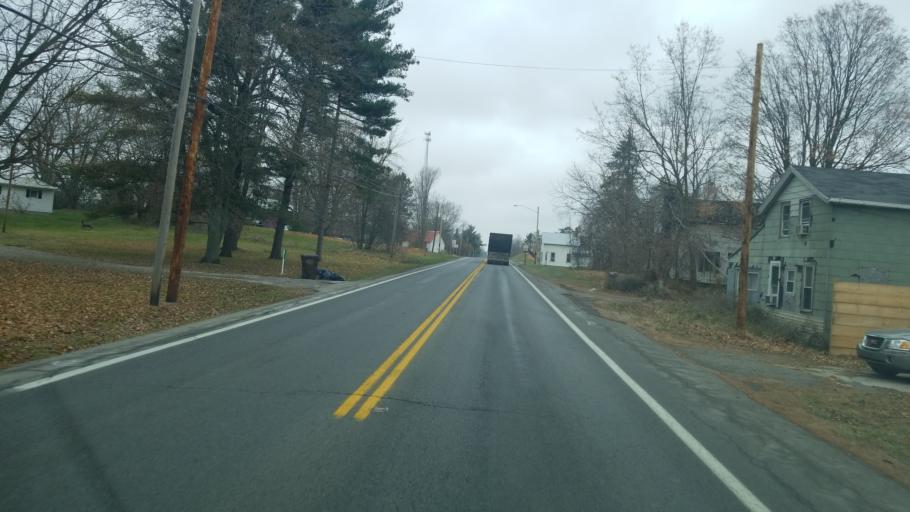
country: US
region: Ohio
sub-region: Huron County
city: Greenwich
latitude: 41.0965
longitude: -82.4899
